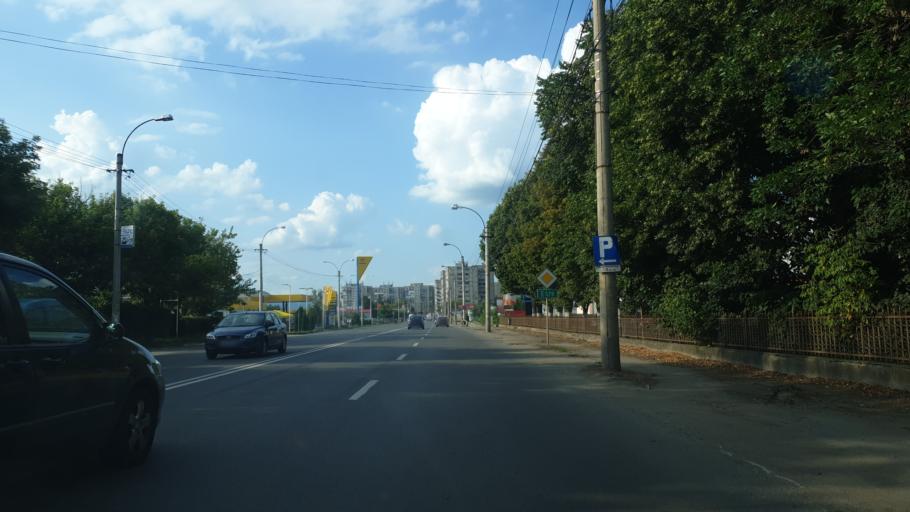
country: RO
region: Covasna
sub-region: Municipiul Sfantu Gheorghe
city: Sfantu-Gheorghe
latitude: 45.8567
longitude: 25.8071
